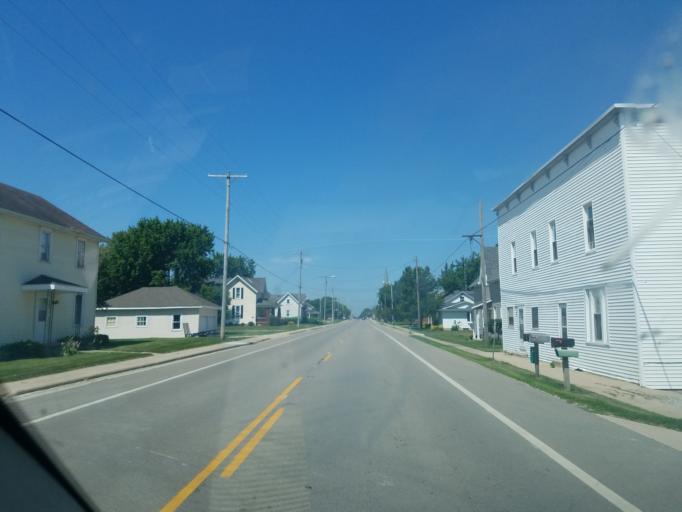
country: US
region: Ohio
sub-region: Auglaize County
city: Minster
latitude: 40.4076
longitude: -84.4672
